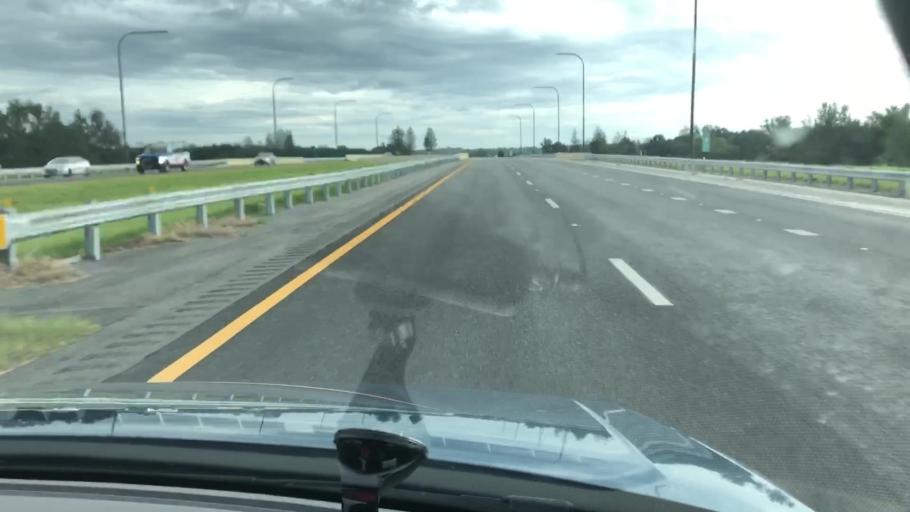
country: US
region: Florida
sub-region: Orange County
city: Zellwood
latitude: 28.7505
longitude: -81.5670
